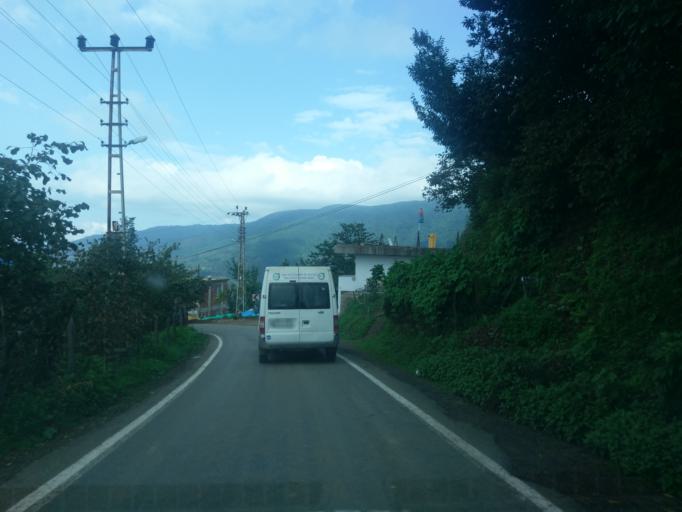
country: TR
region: Ordu
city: Camas
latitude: 40.9071
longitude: 37.6135
